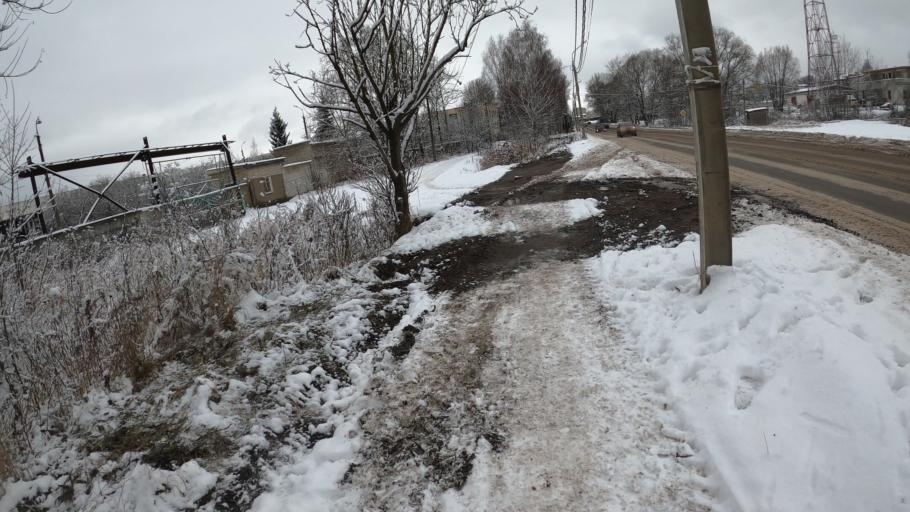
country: RU
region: Jaroslavl
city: Pereslavl'-Zalesskiy
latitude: 56.7392
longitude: 38.8952
